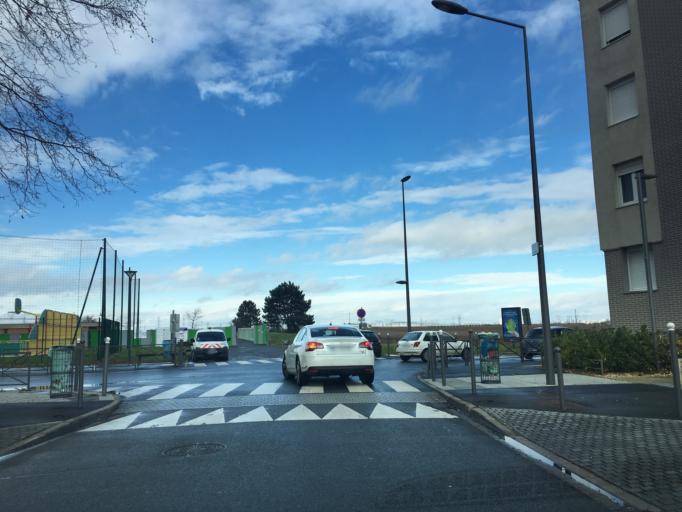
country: FR
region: Ile-de-France
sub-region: Departement du Val-d'Oise
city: Villiers-le-Bel
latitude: 49.0047
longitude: 2.4186
